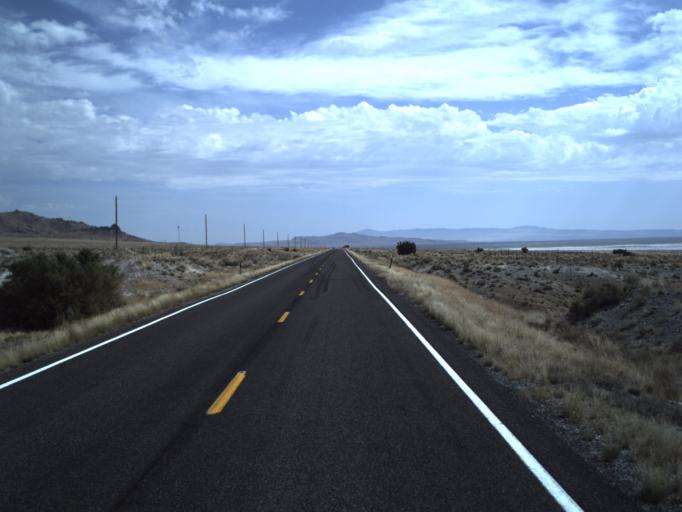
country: US
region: Utah
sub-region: Tooele County
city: Wendover
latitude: 41.4380
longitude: -113.7315
